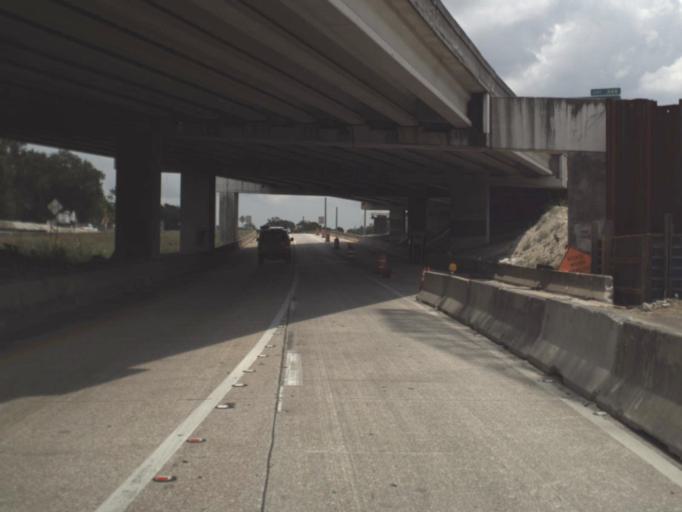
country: US
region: Florida
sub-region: Duval County
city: Jacksonville
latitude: 30.3100
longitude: -81.6479
